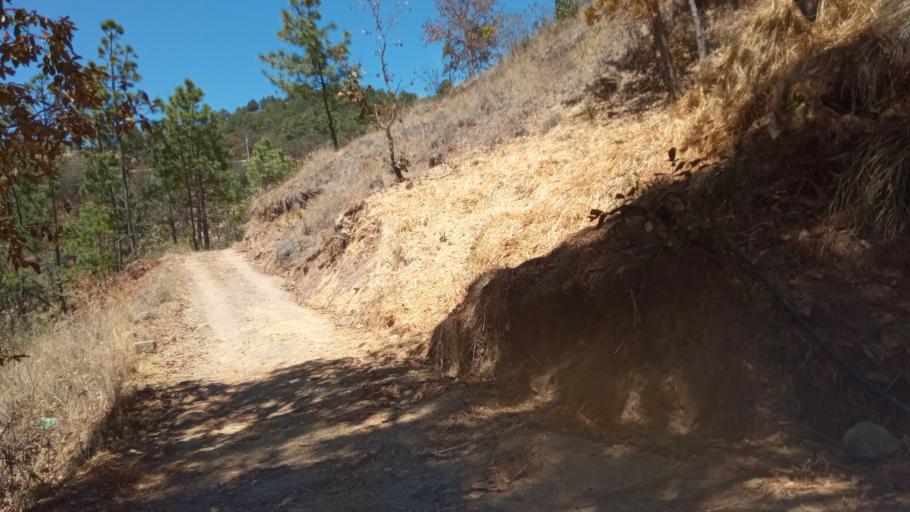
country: GT
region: San Marcos
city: Tejutla
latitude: 15.1353
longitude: -91.7903
